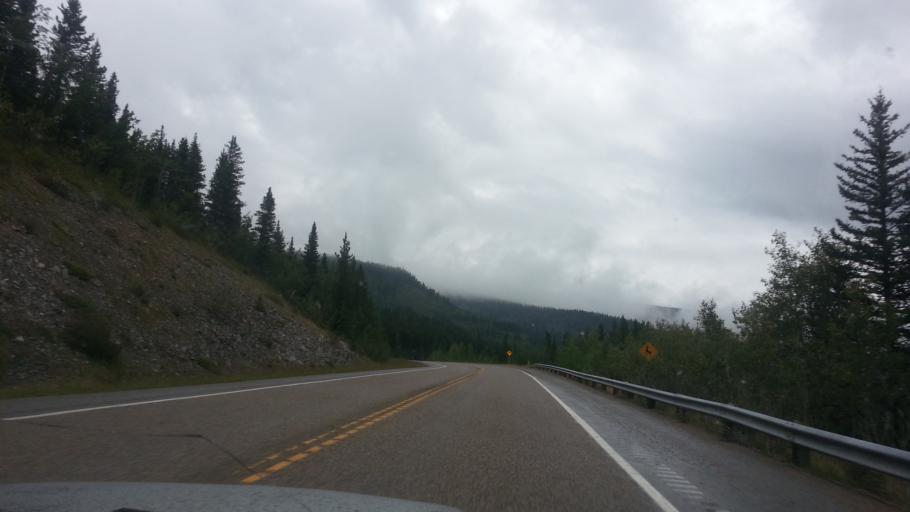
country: CA
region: Alberta
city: Cochrane
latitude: 50.8592
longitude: -114.7959
